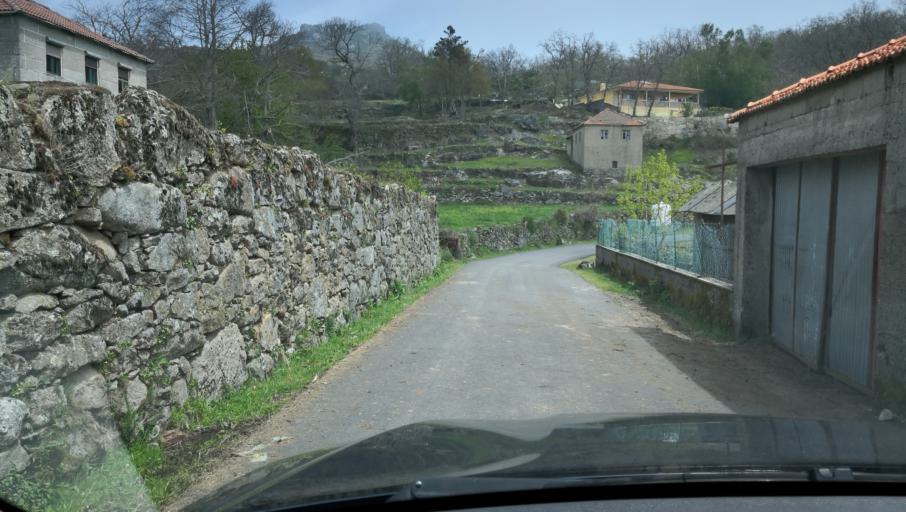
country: PT
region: Vila Real
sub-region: Vila Real
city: Vila Real
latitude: 41.2974
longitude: -7.8311
